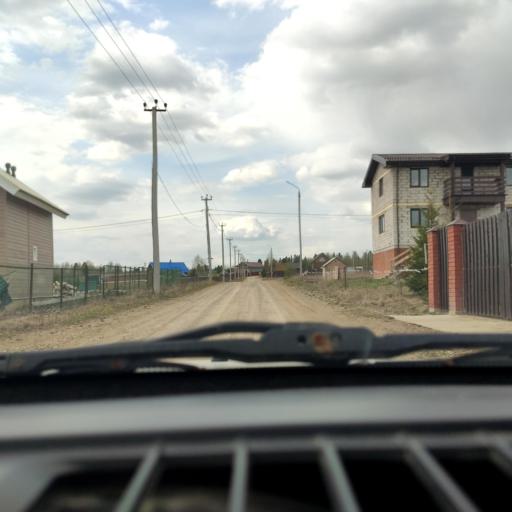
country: RU
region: Perm
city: Polazna
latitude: 58.3534
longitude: 56.2726
